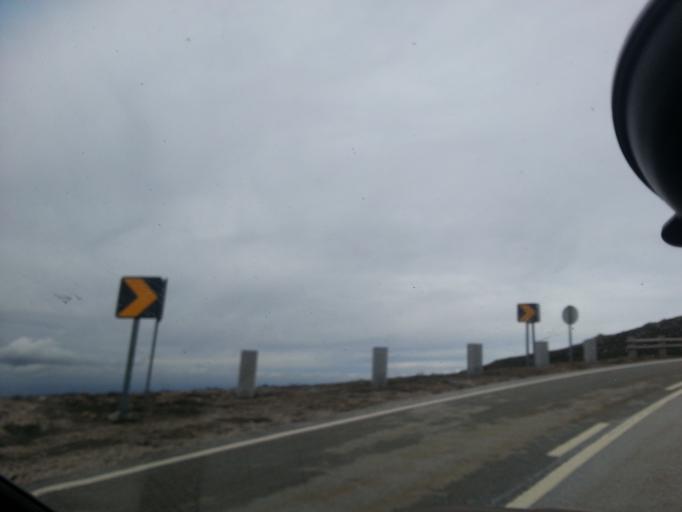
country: PT
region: Guarda
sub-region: Seia
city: Seia
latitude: 40.3499
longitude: -7.6878
